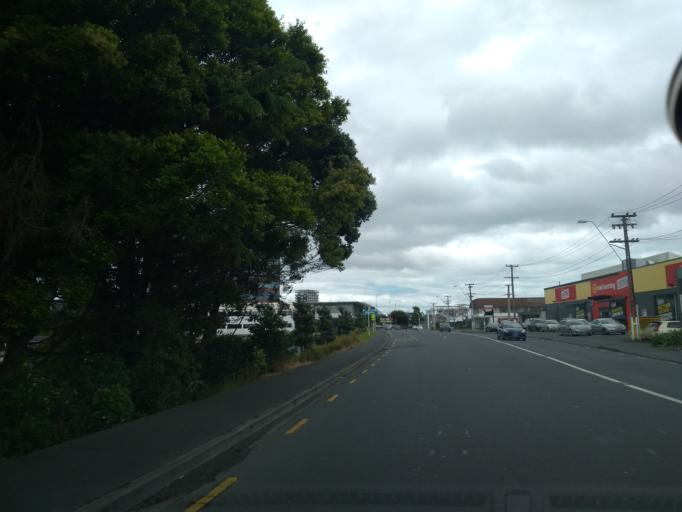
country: NZ
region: Auckland
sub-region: Auckland
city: Tamaki
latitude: -36.9098
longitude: 174.8197
